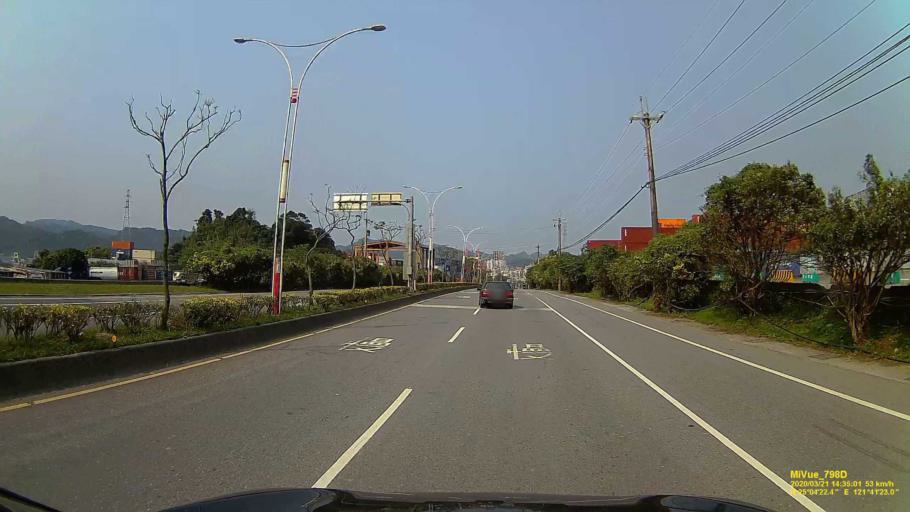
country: TW
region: Taiwan
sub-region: Keelung
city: Keelung
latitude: 25.0730
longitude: 121.6898
